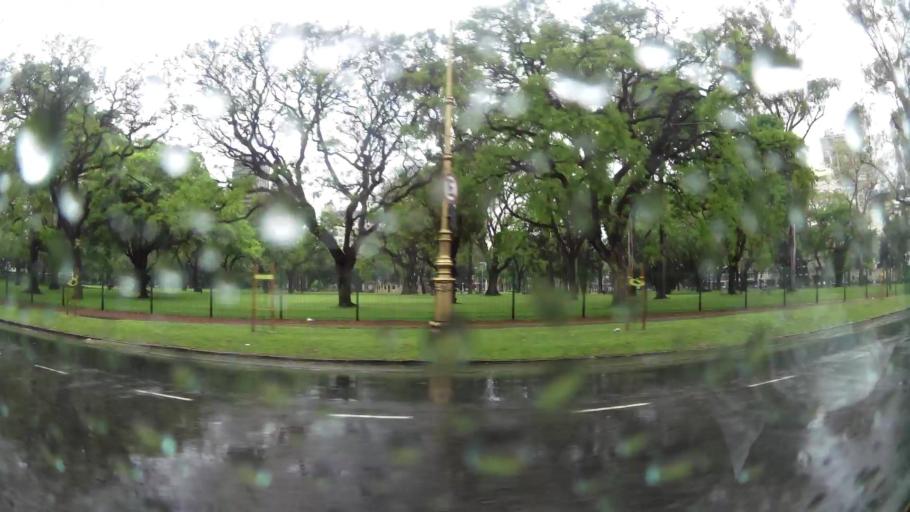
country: AR
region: Buenos Aires F.D.
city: Retiro
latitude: -34.5763
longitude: -58.4095
